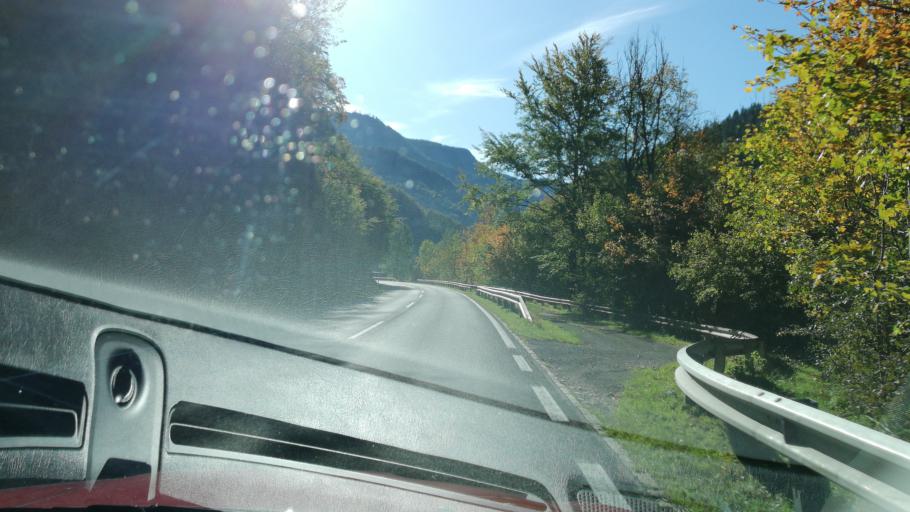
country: AT
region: Upper Austria
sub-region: Politischer Bezirk Steyr-Land
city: Weyer
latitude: 47.8408
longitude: 14.6396
